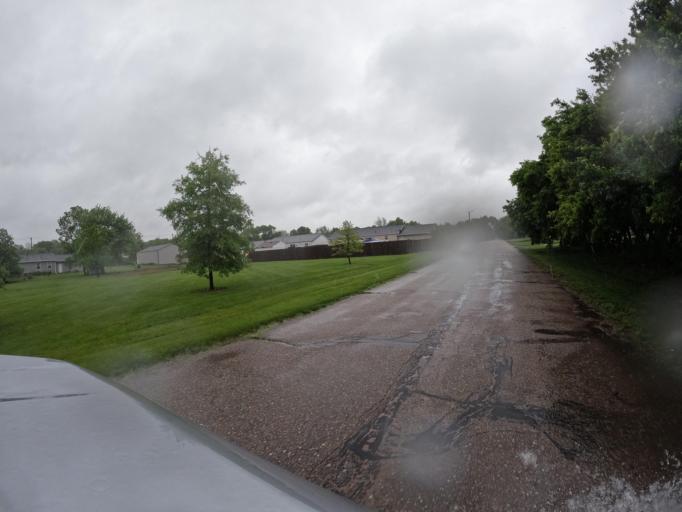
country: US
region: Nebraska
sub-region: Gage County
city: Wymore
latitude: 40.1232
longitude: -96.6753
